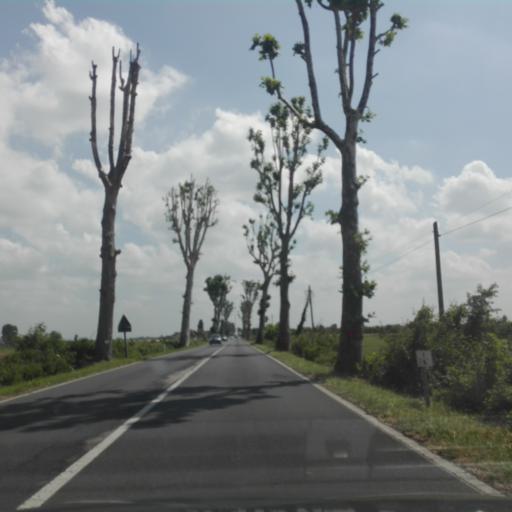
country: IT
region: Veneto
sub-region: Provincia di Rovigo
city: Buso
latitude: 45.0760
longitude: 11.8488
